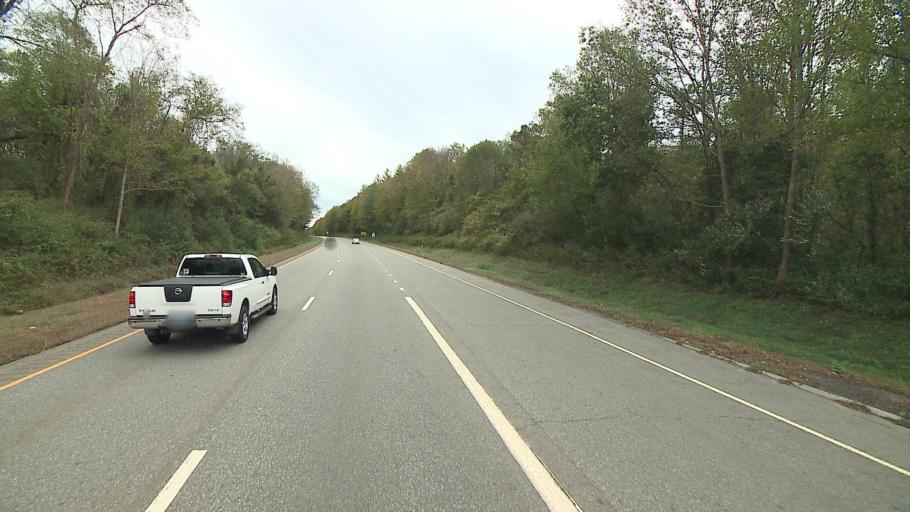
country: US
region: Connecticut
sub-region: Middlesex County
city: Chester Center
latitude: 41.3973
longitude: -72.4710
